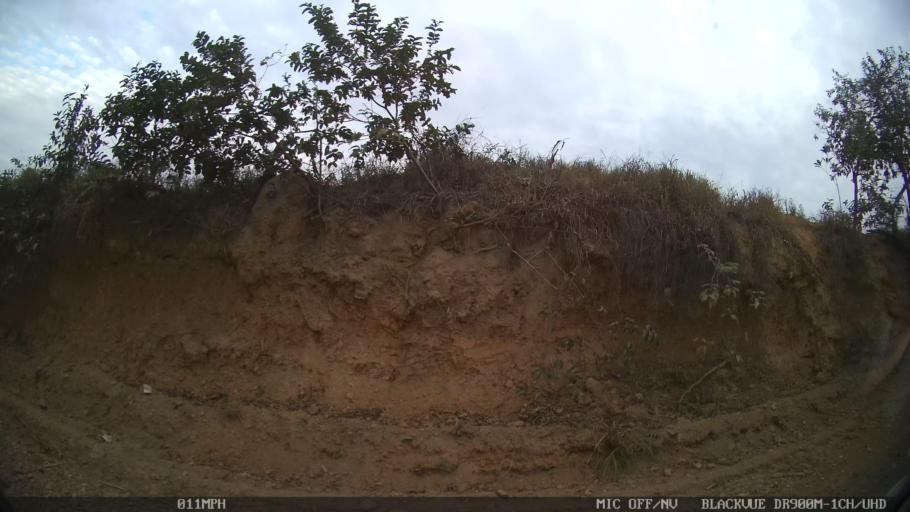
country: BR
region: Sao Paulo
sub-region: Americana
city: Americana
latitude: -22.6794
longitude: -47.3796
